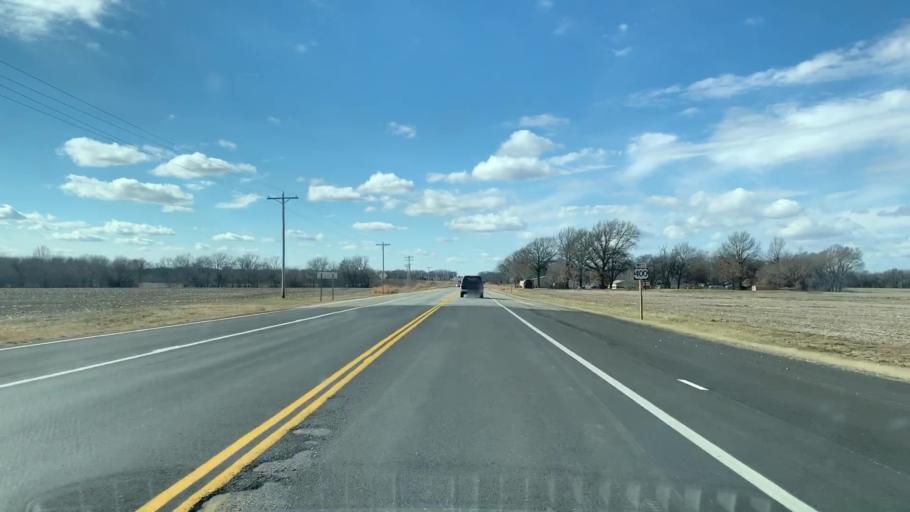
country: US
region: Kansas
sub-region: Labette County
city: Parsons
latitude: 37.3404
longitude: -95.1271
